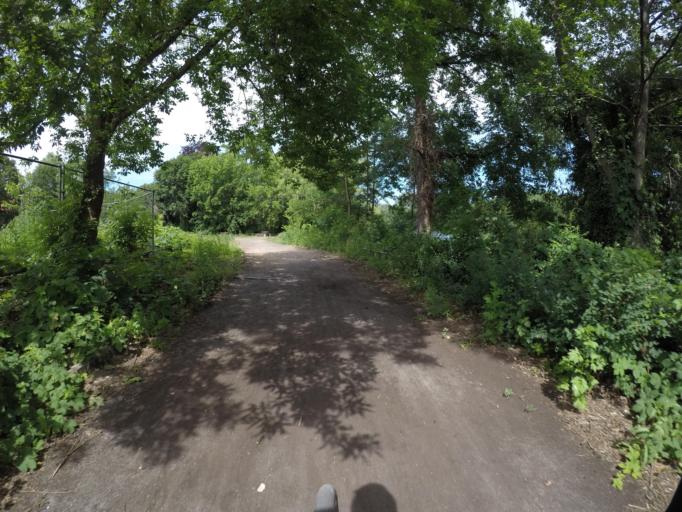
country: DE
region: Berlin
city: Kopenick Bezirk
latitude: 52.4526
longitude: 13.5655
